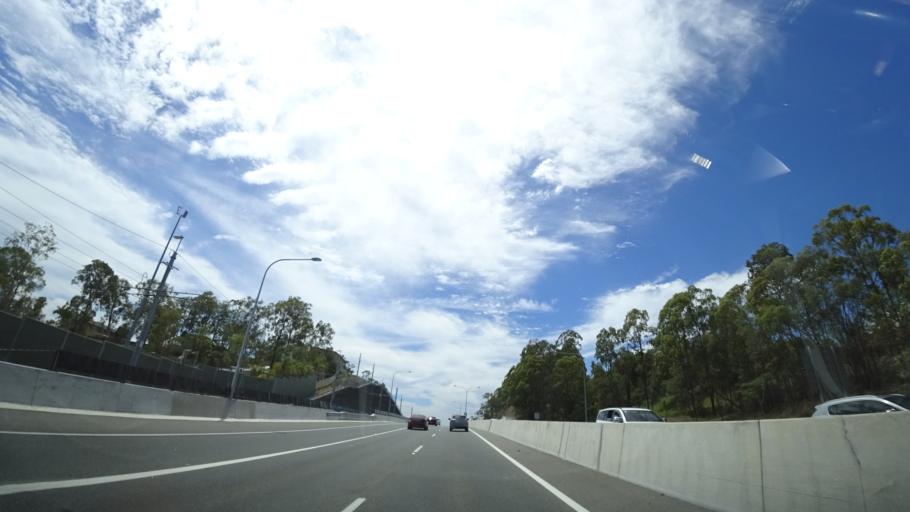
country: AU
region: Queensland
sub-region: Gold Coast
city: Nerang
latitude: -27.9617
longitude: 153.3546
